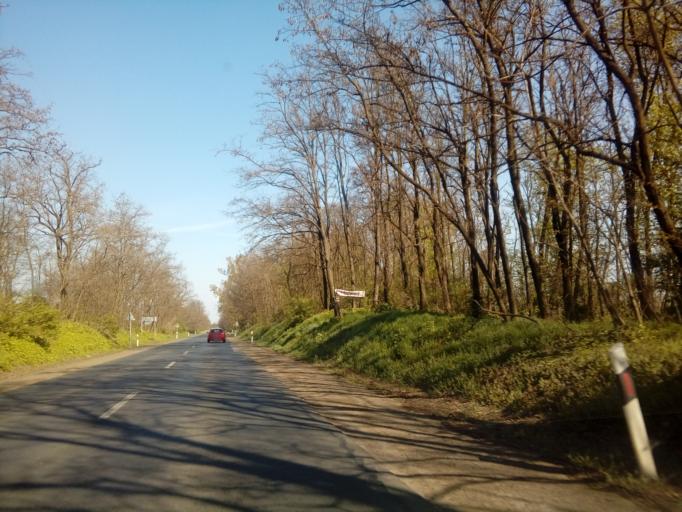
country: HU
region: Szabolcs-Szatmar-Bereg
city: Nyiregyhaza
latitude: 47.9172
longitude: 21.7717
